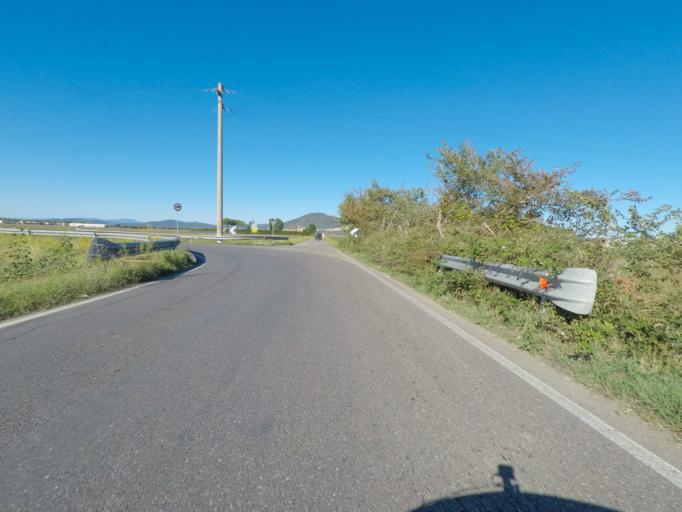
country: IT
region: Tuscany
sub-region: Provincia di Grosseto
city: Grosseto
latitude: 42.7729
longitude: 11.1398
